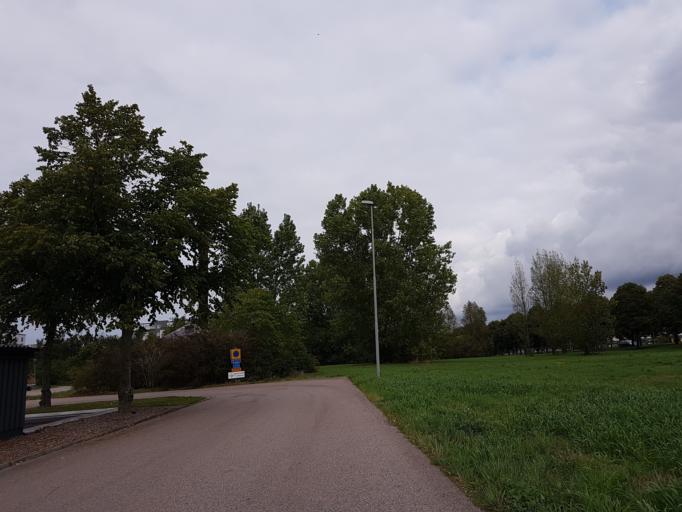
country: SE
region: Skane
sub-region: Landskrona
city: Landskrona
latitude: 55.8909
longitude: 12.8280
